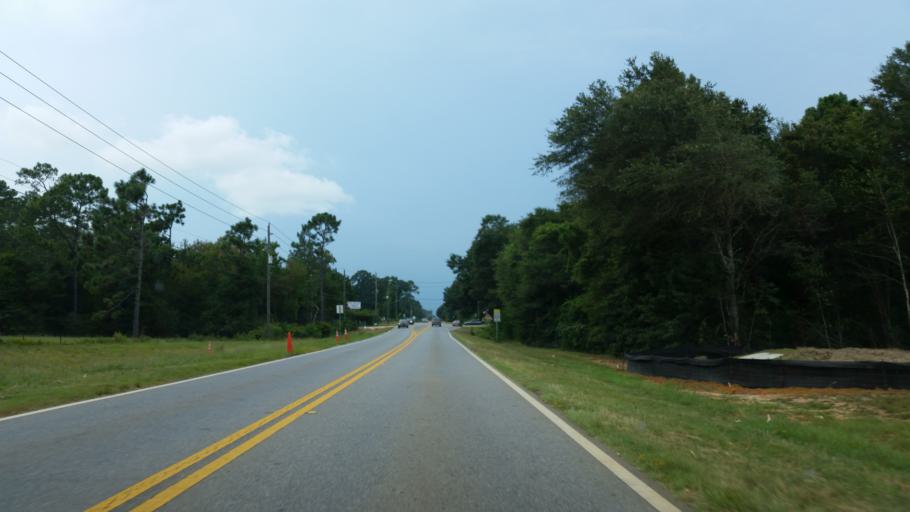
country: US
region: Florida
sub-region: Santa Rosa County
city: Pace
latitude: 30.6323
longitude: -87.1706
